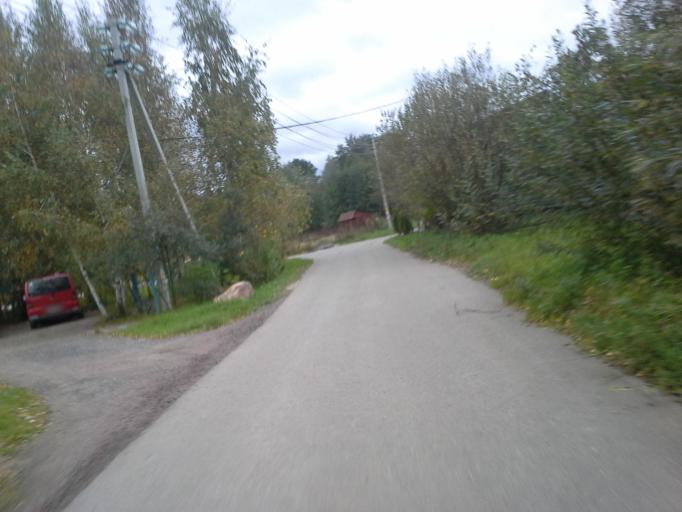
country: RU
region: Moskovskaya
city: Kokoshkino
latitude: 55.6130
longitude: 37.1430
